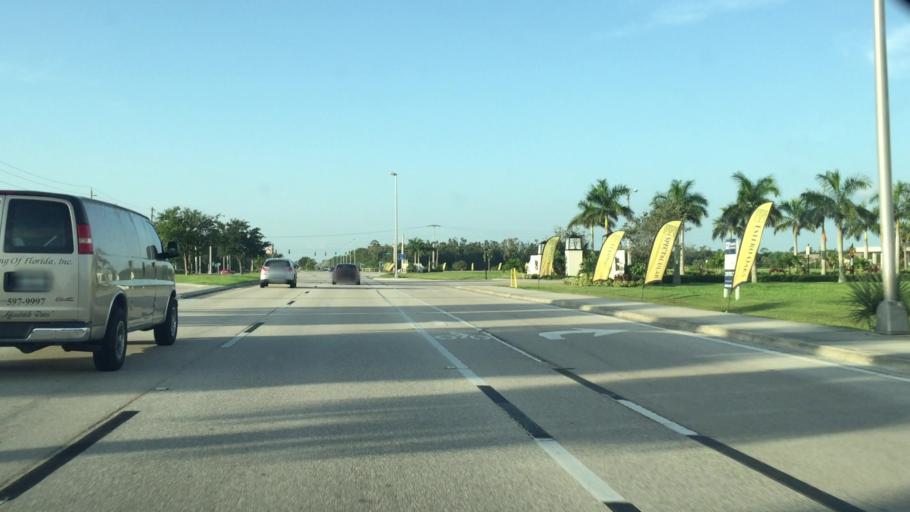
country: US
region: Florida
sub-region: Lee County
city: Three Oaks
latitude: 26.4519
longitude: -81.7890
